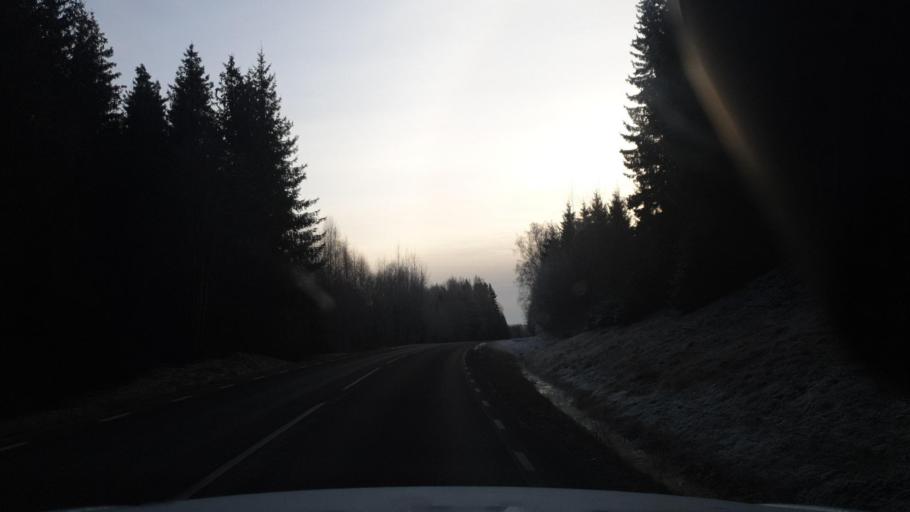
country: SE
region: Vaermland
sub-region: Eda Kommun
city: Amotfors
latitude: 59.7311
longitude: 12.4181
